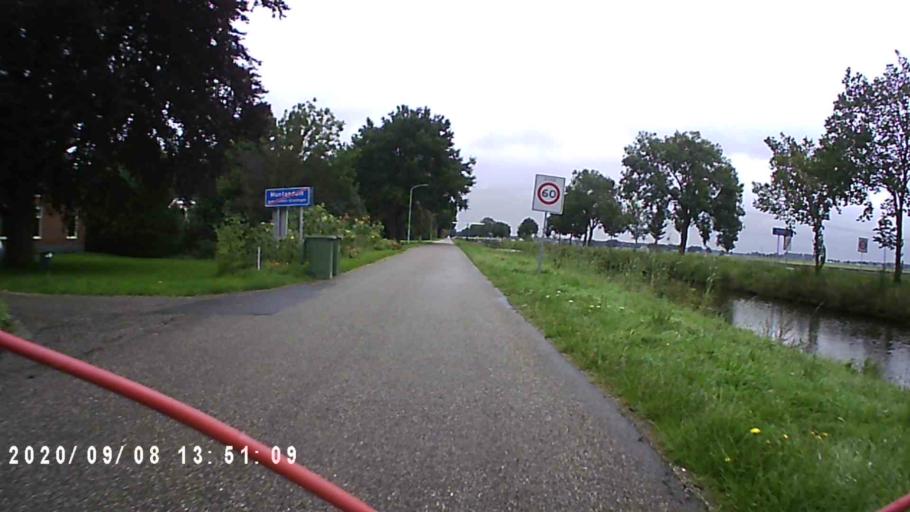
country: NL
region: Groningen
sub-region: Gemeente Veendam
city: Veendam
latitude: 53.1407
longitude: 6.8673
